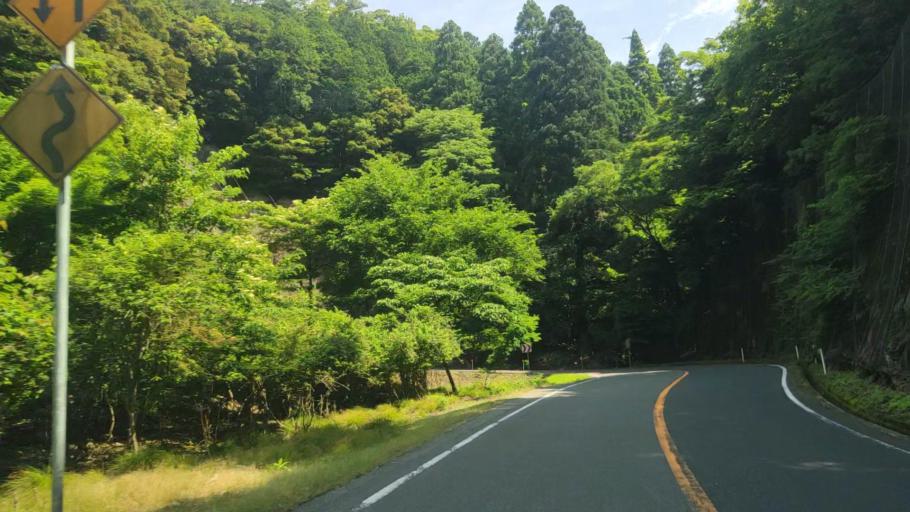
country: JP
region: Hyogo
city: Toyooka
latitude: 35.6360
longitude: 134.7807
